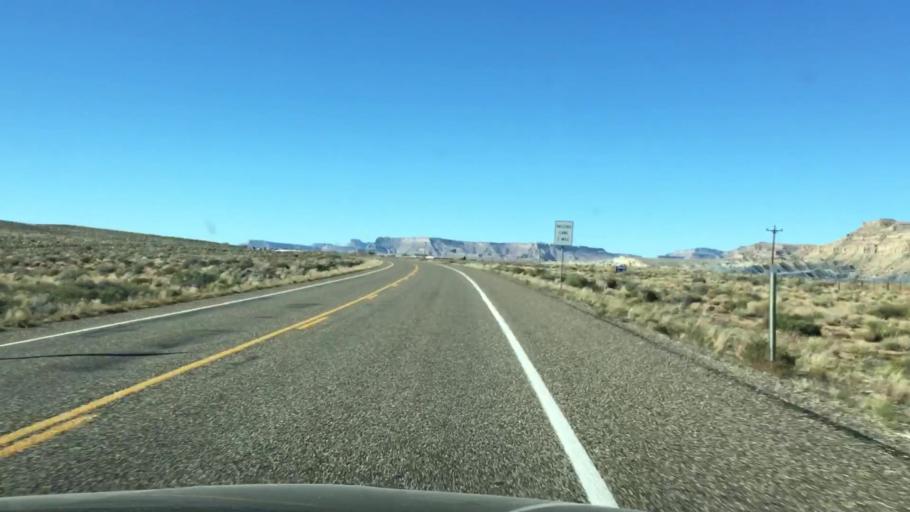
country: US
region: Arizona
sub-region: Coconino County
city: Page
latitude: 37.0700
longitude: -111.6501
